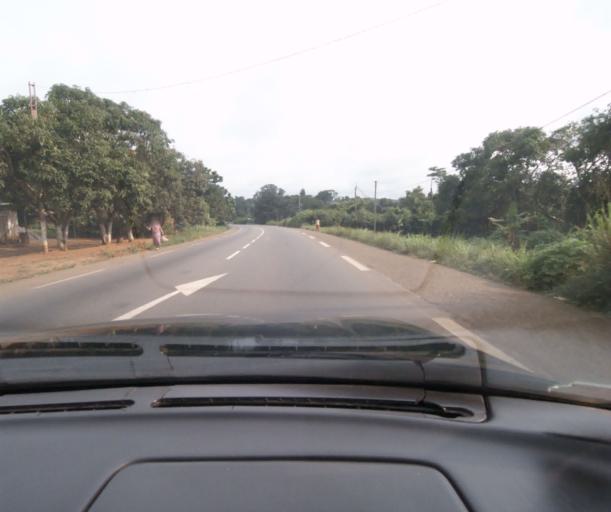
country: CM
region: Centre
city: Obala
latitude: 4.0834
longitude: 11.5486
